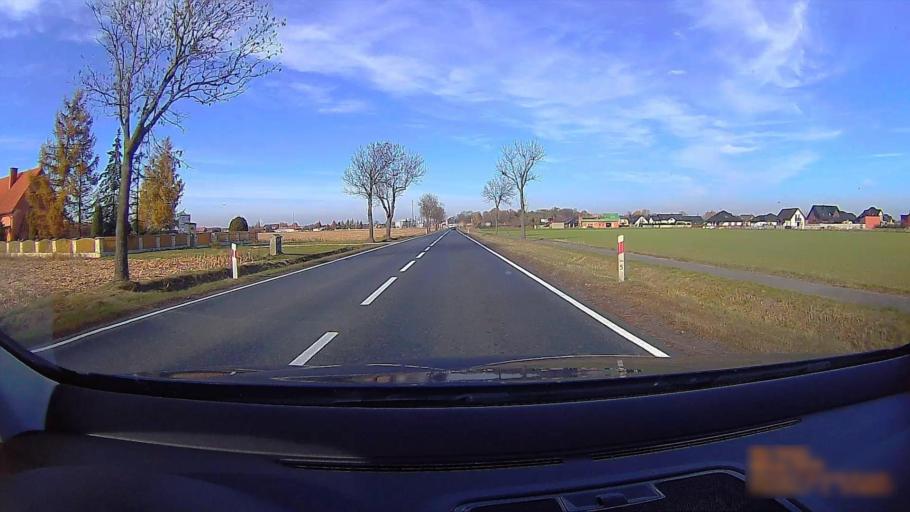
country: PL
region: Greater Poland Voivodeship
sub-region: Powiat koninski
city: Rychwal
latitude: 52.0615
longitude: 18.1637
